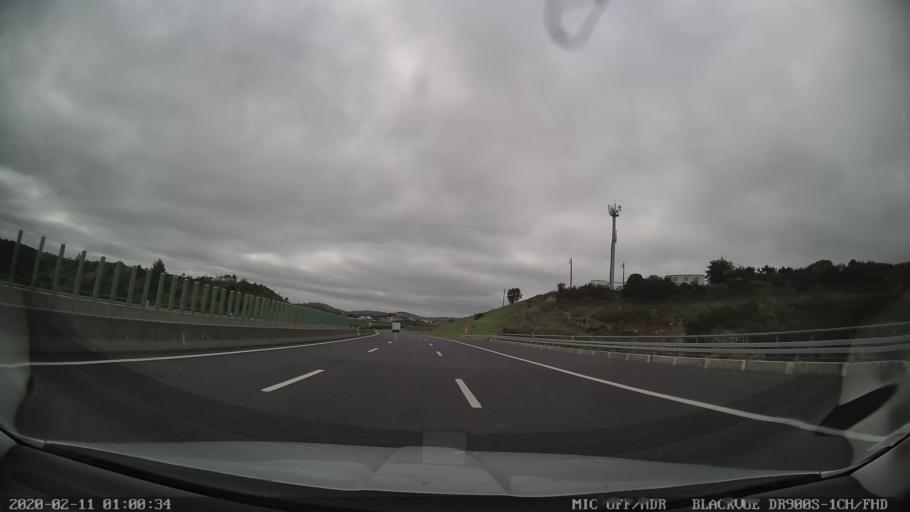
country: PT
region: Lisbon
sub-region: Loures
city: Bucelas
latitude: 38.9240
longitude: -9.0760
